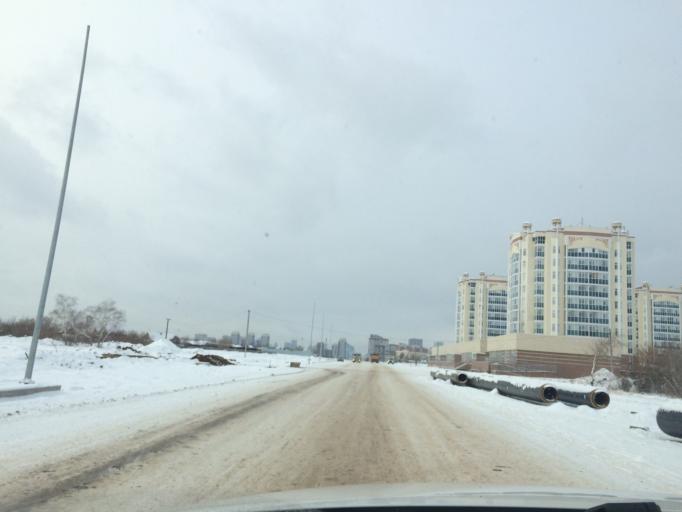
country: KZ
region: Astana Qalasy
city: Astana
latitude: 51.1187
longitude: 71.5071
